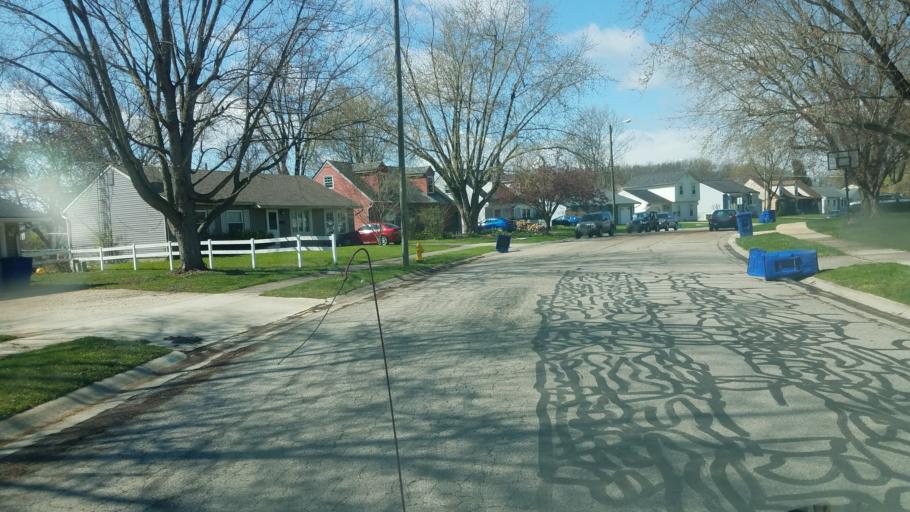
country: US
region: Ohio
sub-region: Delaware County
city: Delaware
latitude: 40.2952
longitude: -83.0902
